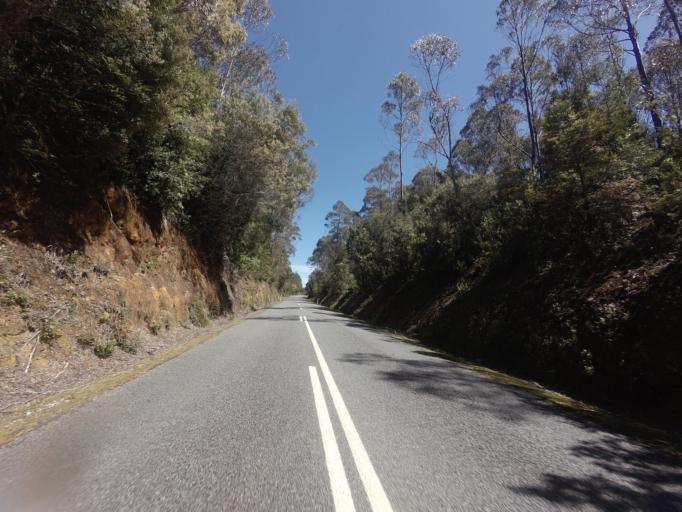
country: AU
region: Tasmania
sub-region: Huon Valley
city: Geeveston
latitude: -42.8167
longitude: 146.3634
